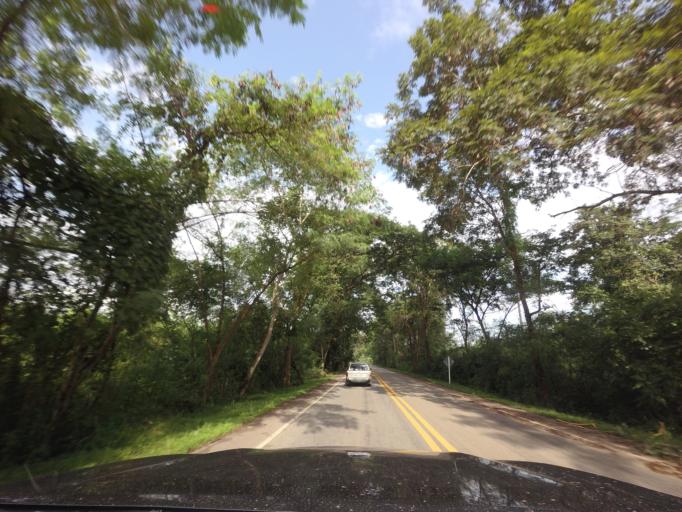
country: TH
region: Nong Khai
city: Pho Tak
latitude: 17.7838
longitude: 102.3745
